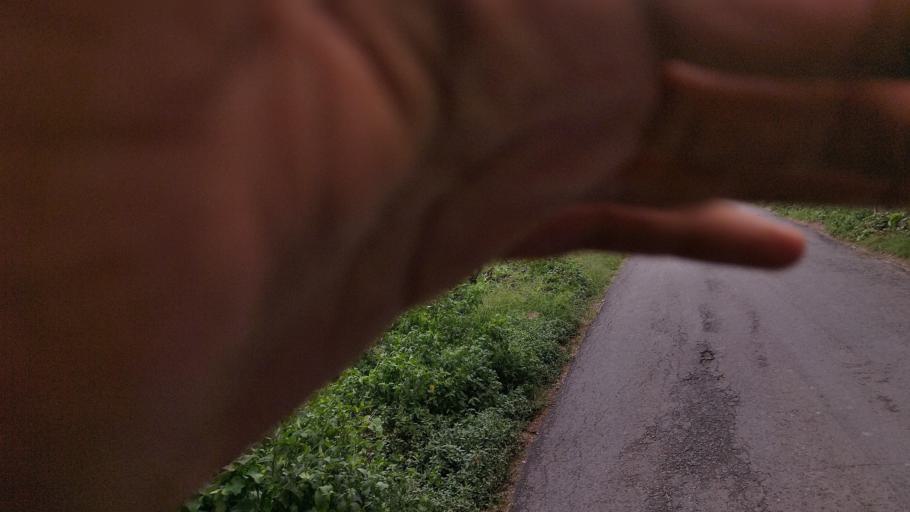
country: BD
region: Dhaka
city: Azimpur
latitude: 23.6823
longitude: 90.3498
